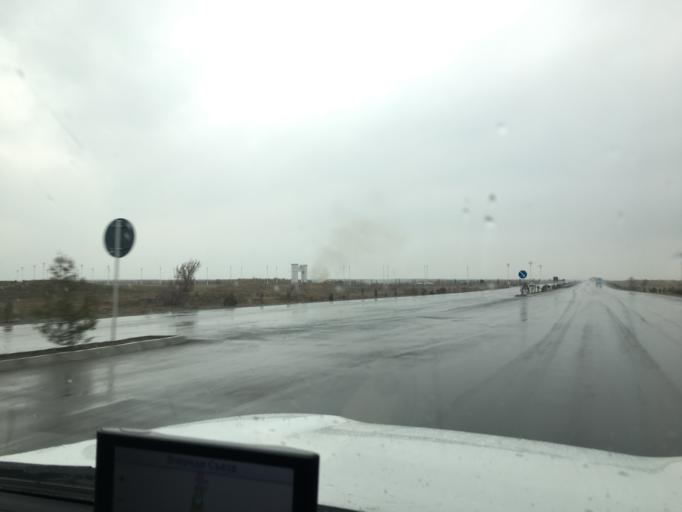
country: TM
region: Ahal
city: Annau
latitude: 37.8617
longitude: 58.6767
